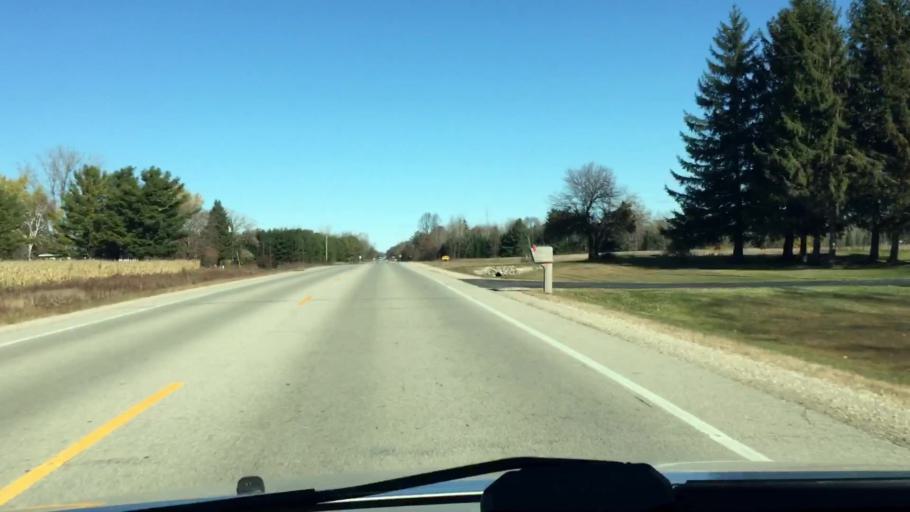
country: US
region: Wisconsin
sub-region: Brown County
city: Pulaski
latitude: 44.7493
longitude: -88.2494
